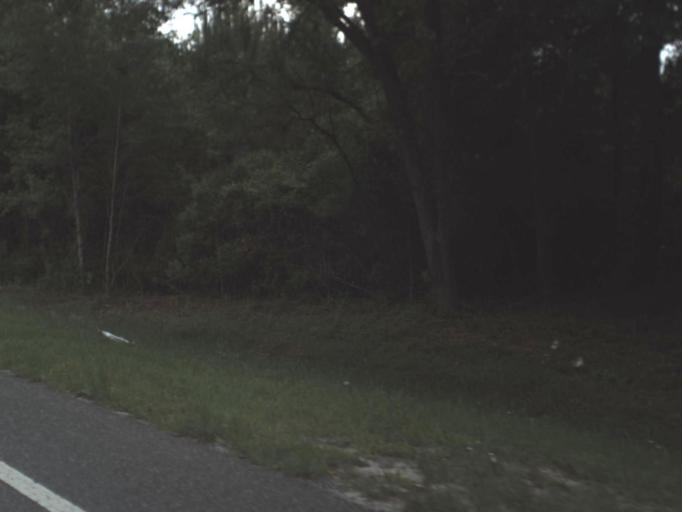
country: US
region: Florida
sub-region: Columbia County
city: Five Points
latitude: 30.2537
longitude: -82.6381
